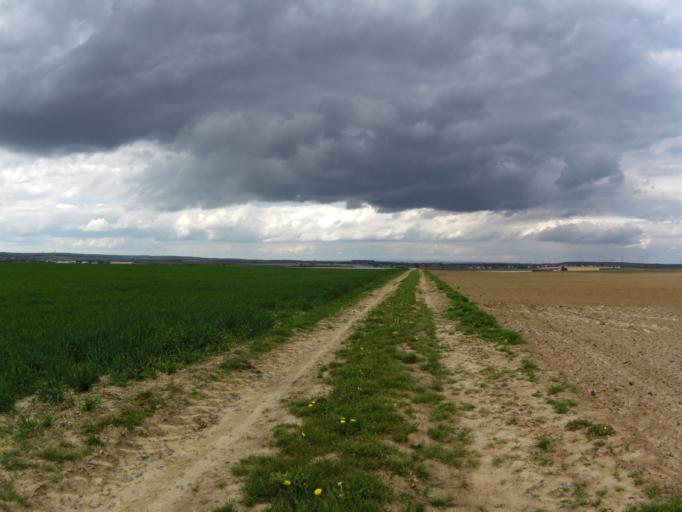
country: DE
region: Bavaria
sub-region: Regierungsbezirk Unterfranken
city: Oberpleichfeld
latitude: 49.8538
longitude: 10.0839
